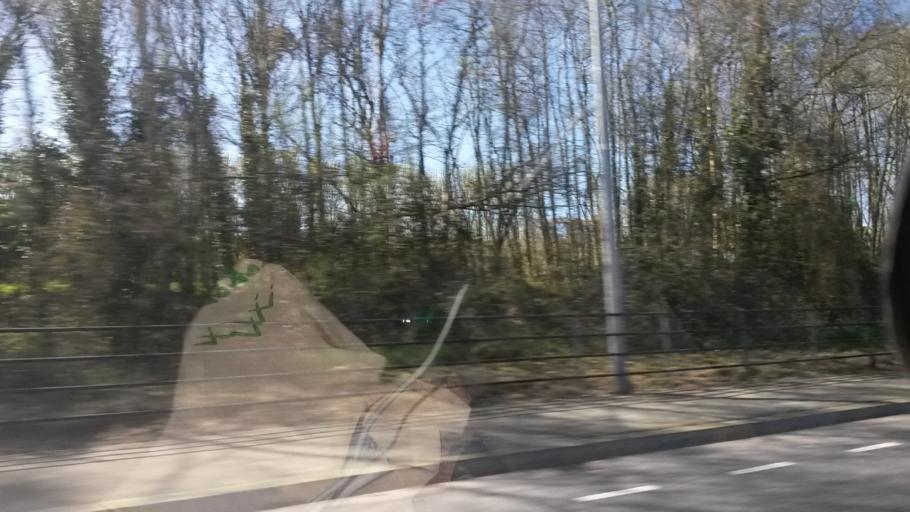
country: IE
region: Munster
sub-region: County Cork
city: Cork
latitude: 51.8940
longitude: -8.5179
